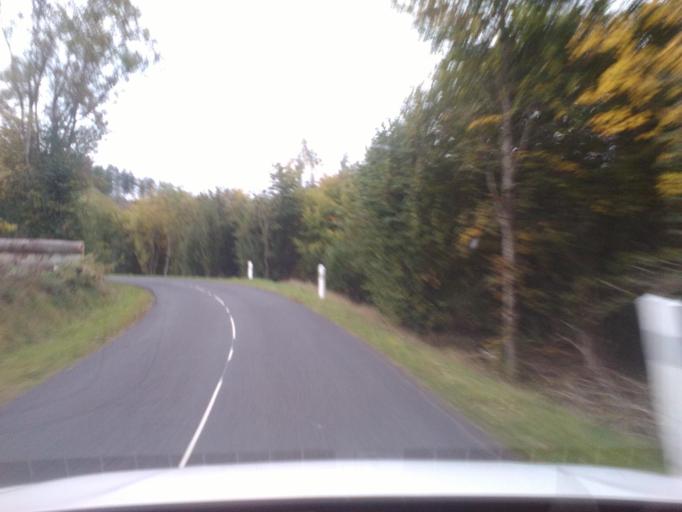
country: FR
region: Lorraine
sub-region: Departement des Vosges
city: Senones
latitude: 48.3776
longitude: 7.0421
